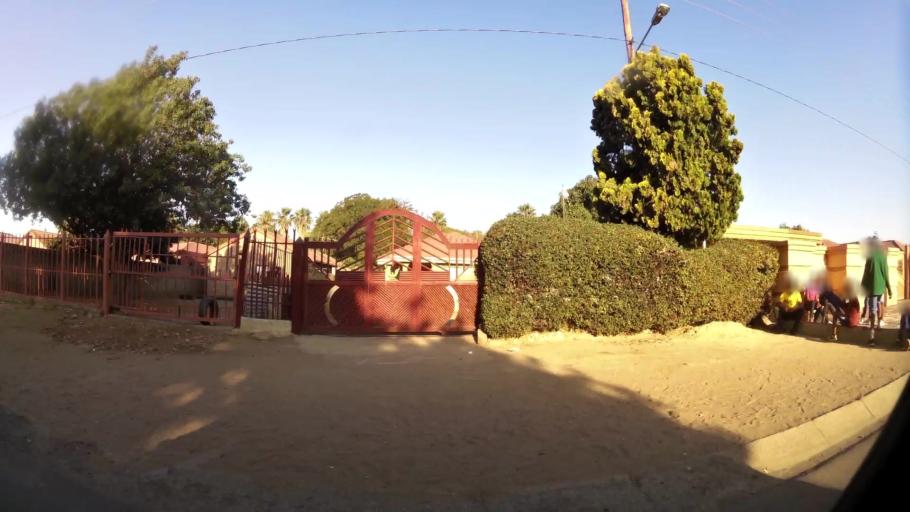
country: ZA
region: North-West
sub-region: Bojanala Platinum District Municipality
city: Rustenburg
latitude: -25.6433
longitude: 27.2248
